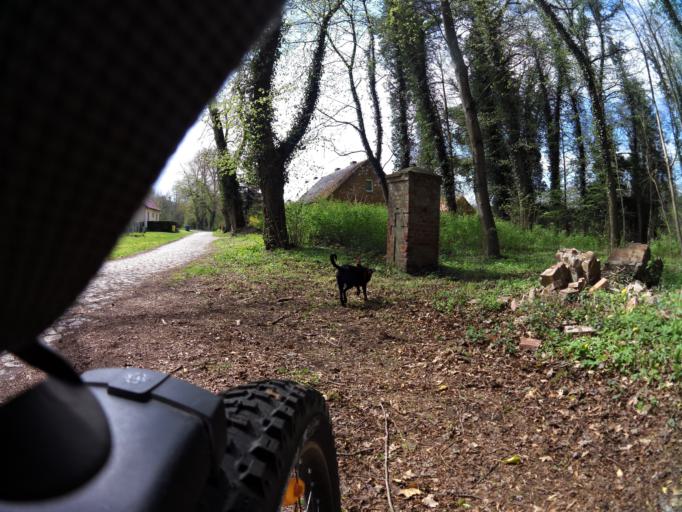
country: PL
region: West Pomeranian Voivodeship
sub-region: Powiat gryficki
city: Ploty
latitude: 53.7497
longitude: 15.3193
